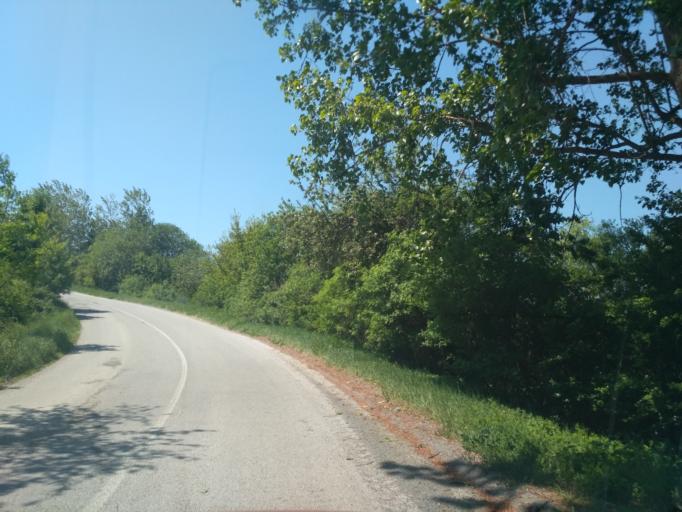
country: SK
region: Kosicky
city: Kosice
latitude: 48.8079
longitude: 21.4008
